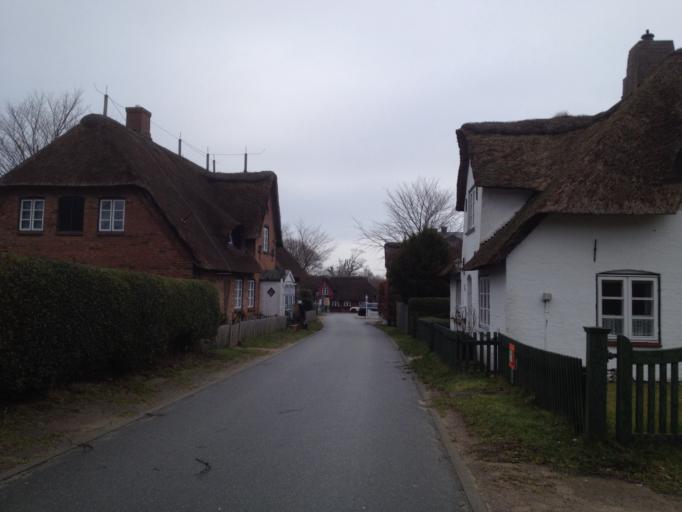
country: DE
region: Schleswig-Holstein
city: Nebel
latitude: 54.6511
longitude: 8.3545
